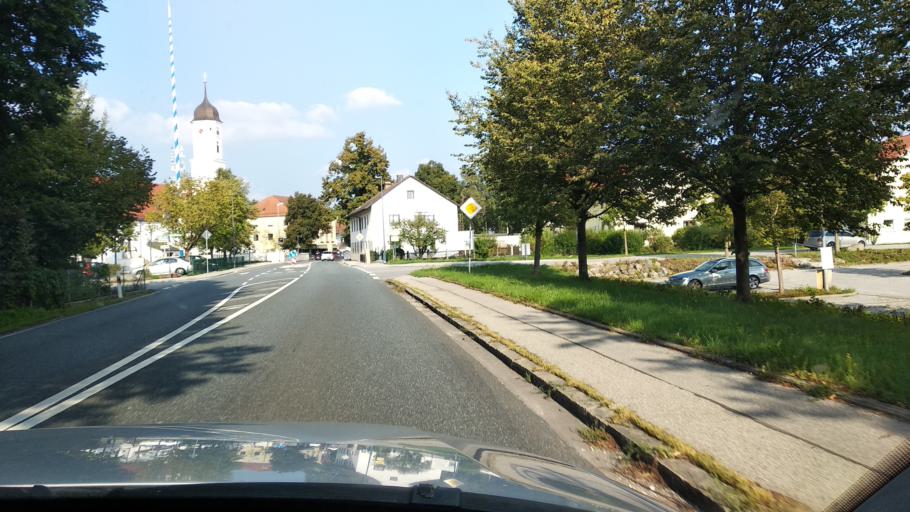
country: DE
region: Bavaria
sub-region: Upper Bavaria
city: Steinhoring
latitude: 48.0862
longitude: 12.0290
